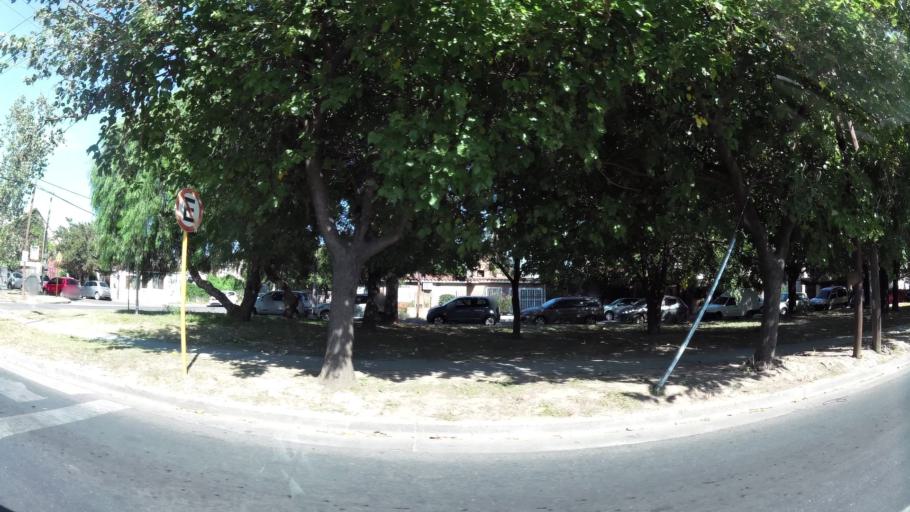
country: AR
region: Cordoba
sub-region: Departamento de Capital
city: Cordoba
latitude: -31.4605
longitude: -64.1868
